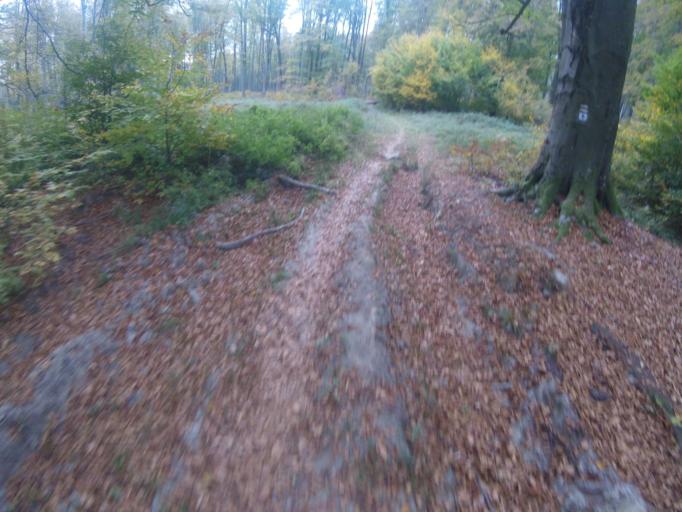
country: HU
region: Veszprem
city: Zirc
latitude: 47.2761
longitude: 17.7568
